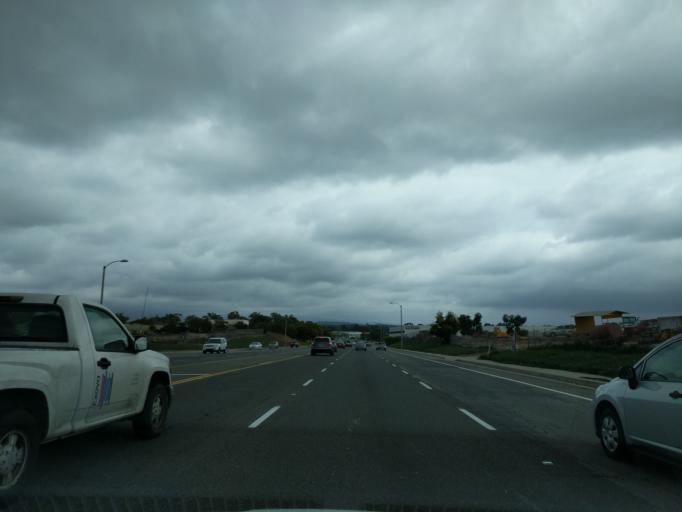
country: US
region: California
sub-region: Orange County
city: Laguna Woods
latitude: 33.6387
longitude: -117.7264
